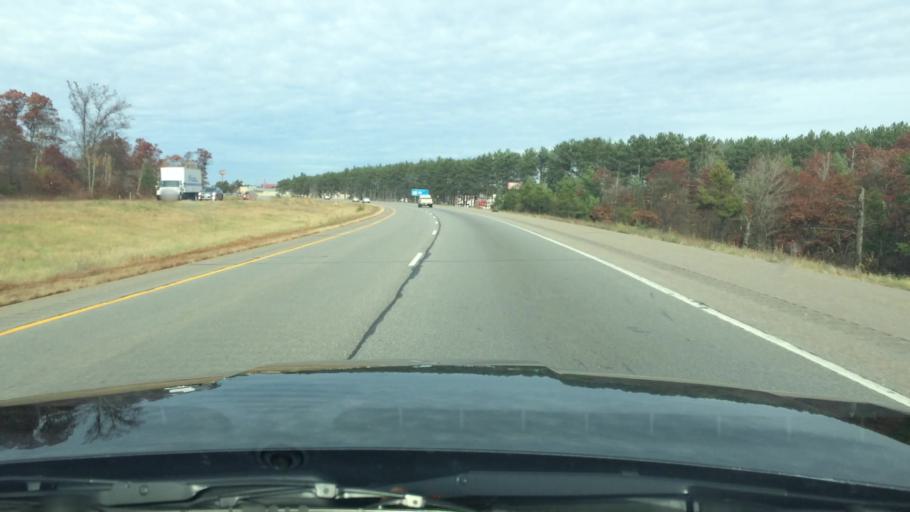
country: US
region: Wisconsin
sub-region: Marathon County
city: Evergreen
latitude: 44.8522
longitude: -89.6381
